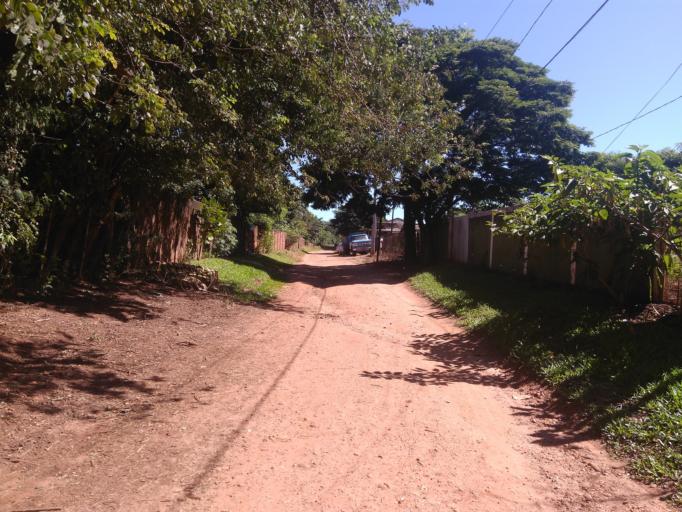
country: BR
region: Mato Grosso do Sul
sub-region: Ponta Pora
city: Ponta Pora
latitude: -22.5027
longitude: -55.7324
